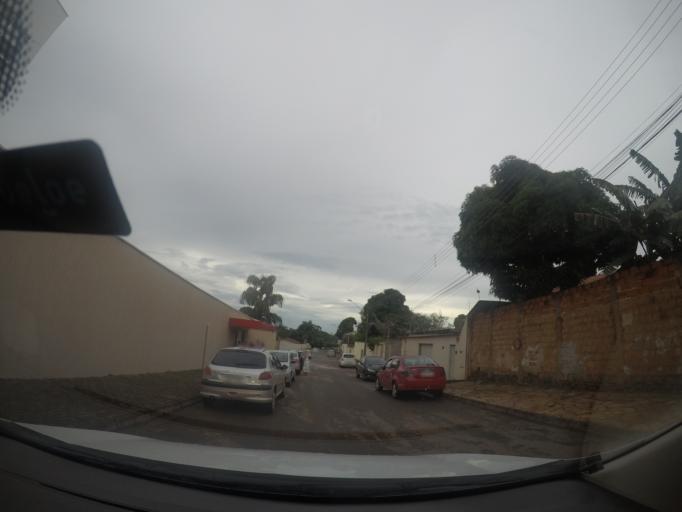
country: BR
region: Goias
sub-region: Goiania
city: Goiania
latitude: -16.6288
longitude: -49.2353
